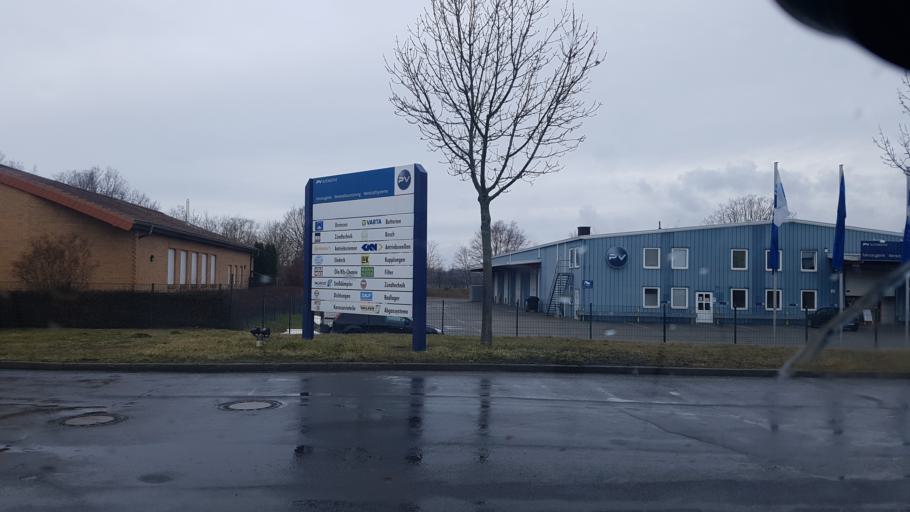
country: DE
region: Brandenburg
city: Cottbus
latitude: 51.7182
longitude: 14.3106
